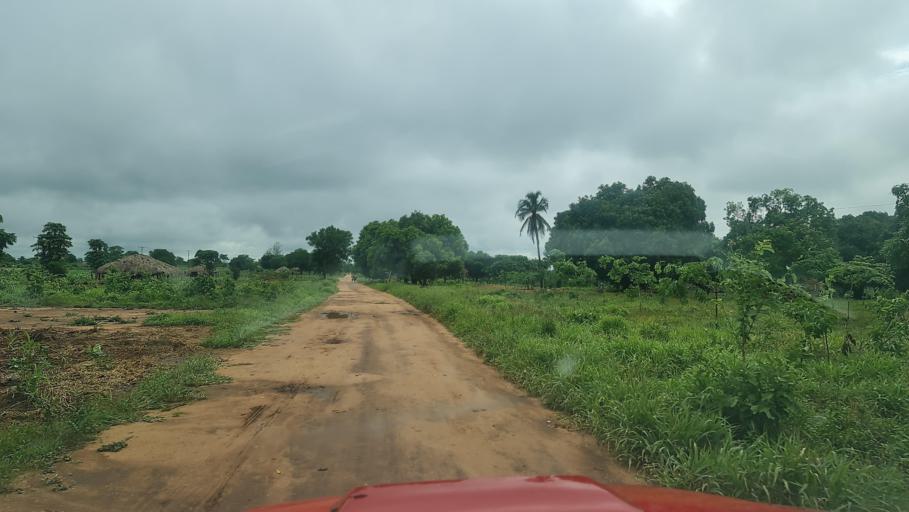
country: MW
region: Southern Region
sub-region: Nsanje District
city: Nsanje
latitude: -17.1796
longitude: 35.8945
